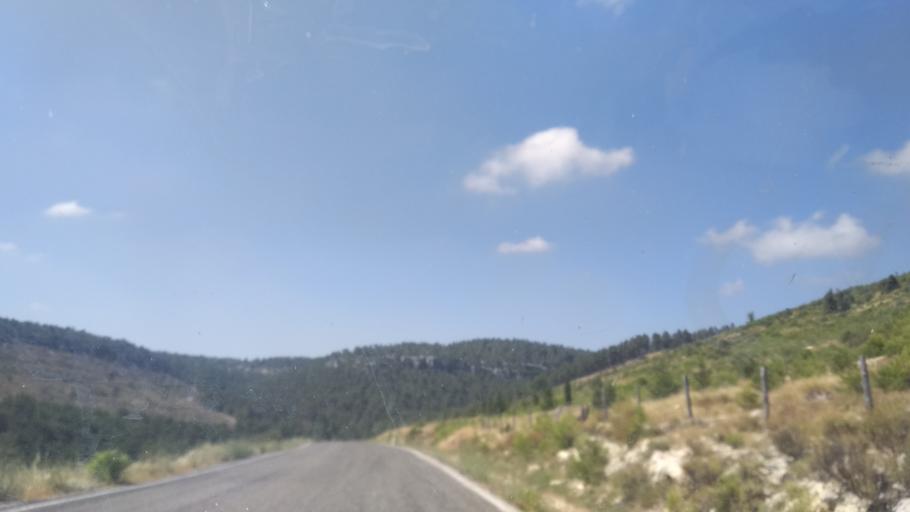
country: TR
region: Mersin
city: Gulnar
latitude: 36.3047
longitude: 33.4554
